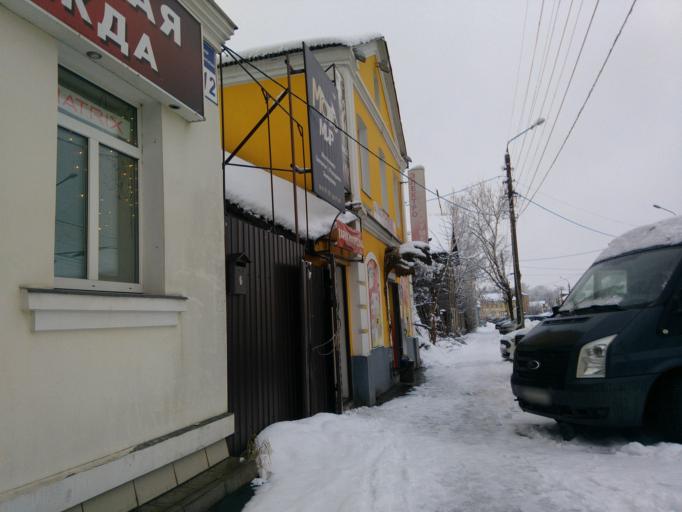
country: RU
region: Tverskaya
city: Torzhok
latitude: 57.0451
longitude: 34.9691
